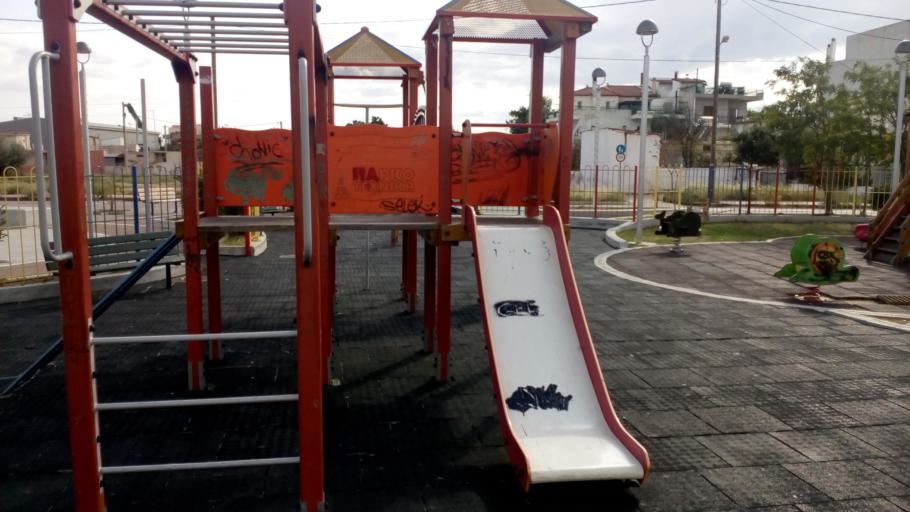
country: GR
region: Attica
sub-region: Nomarchia Dytikis Attikis
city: Elefsina
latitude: 38.0576
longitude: 23.5302
